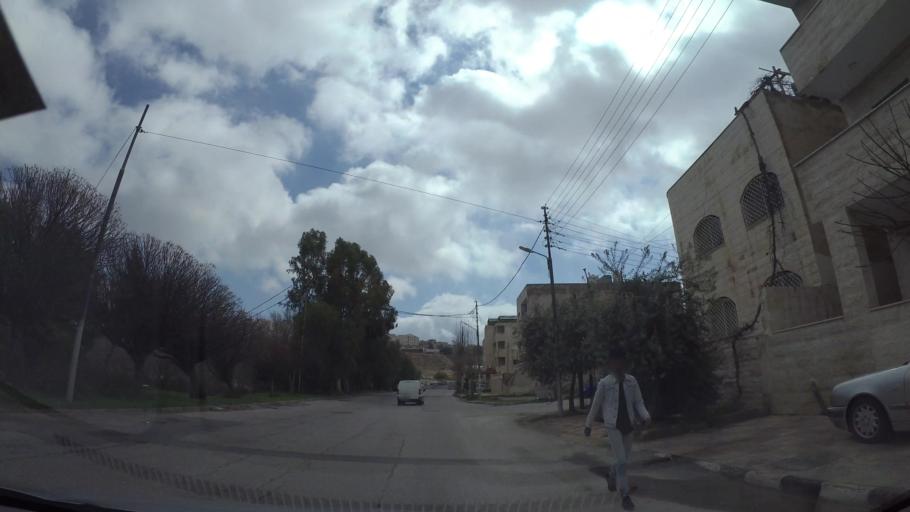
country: JO
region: Amman
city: Al Jubayhah
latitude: 32.0657
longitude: 35.8855
